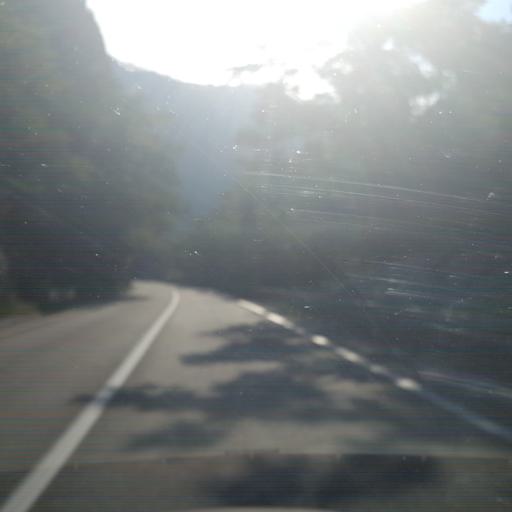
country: RS
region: Central Serbia
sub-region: Nisavski Okrug
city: Svrljig
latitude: 43.3228
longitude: 22.1675
